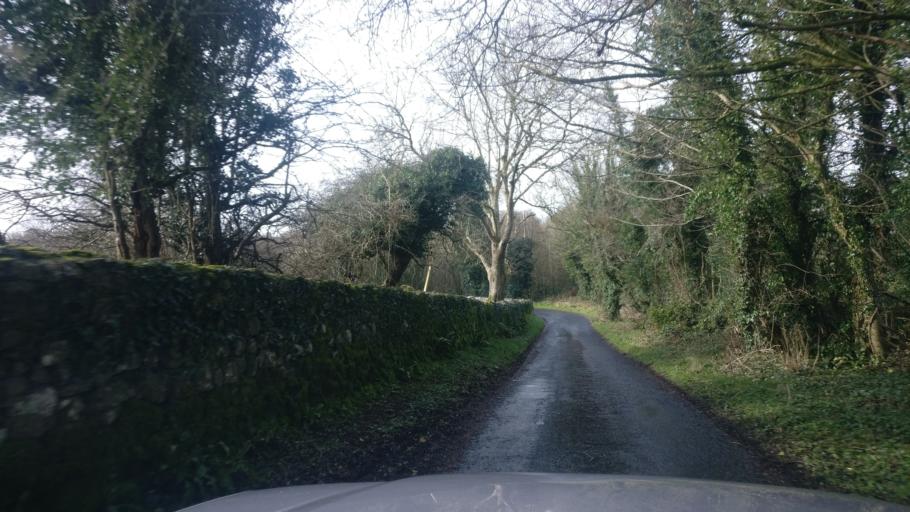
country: IE
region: Connaught
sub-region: County Galway
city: Loughrea
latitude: 53.2835
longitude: -8.5960
